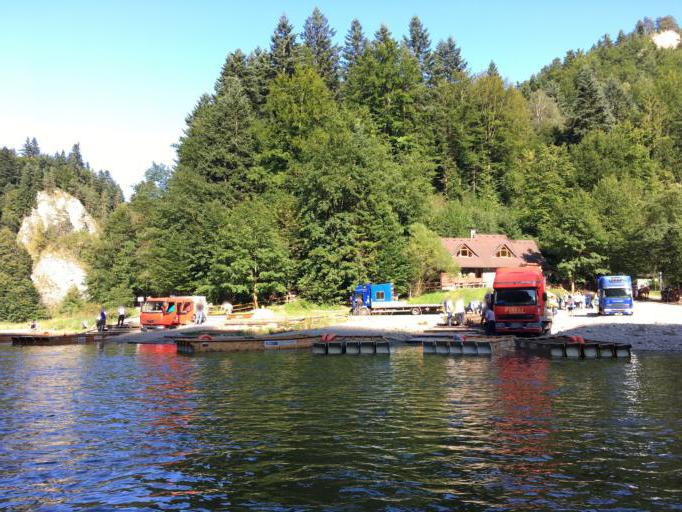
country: PL
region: Lesser Poland Voivodeship
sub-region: Powiat nowotarski
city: Kroscienko nad Dunajcem
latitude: 49.4160
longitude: 20.4456
